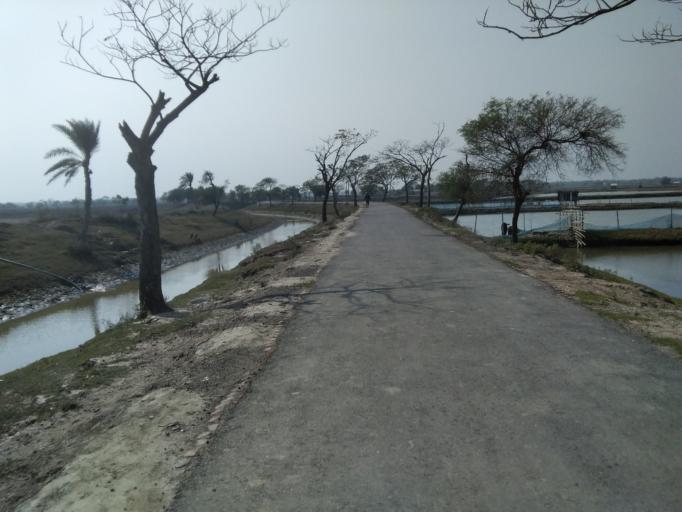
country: BD
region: Khulna
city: Satkhira
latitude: 22.6338
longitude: 89.0159
